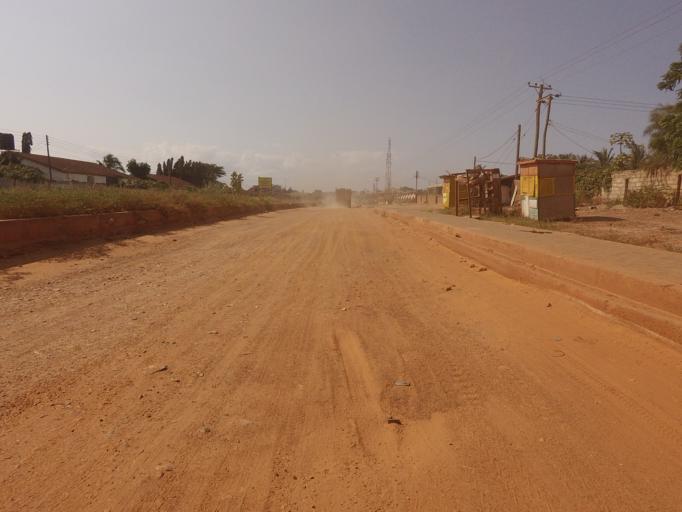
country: GH
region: Greater Accra
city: Teshi Old Town
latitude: 5.6234
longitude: -0.1243
